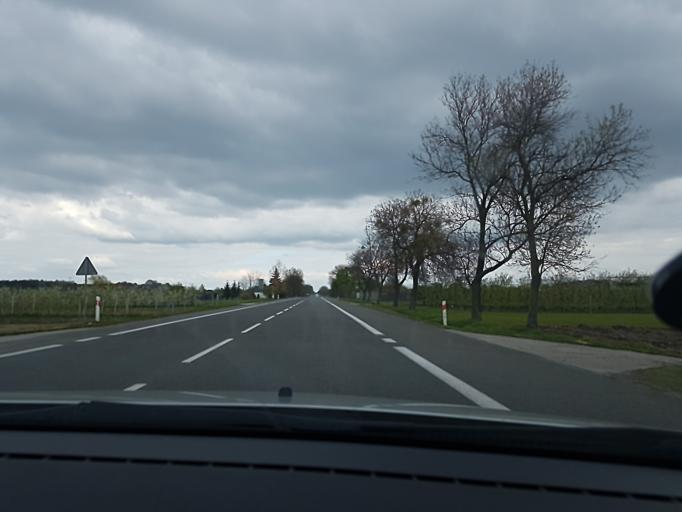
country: PL
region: Lodz Voivodeship
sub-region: powiat Lowicki
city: Nieborow
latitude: 52.1385
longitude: 20.0628
